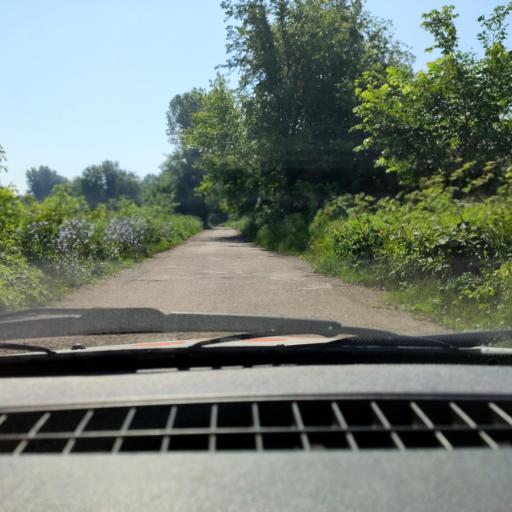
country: RU
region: Bashkortostan
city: Ufa
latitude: 54.6588
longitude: 55.9686
